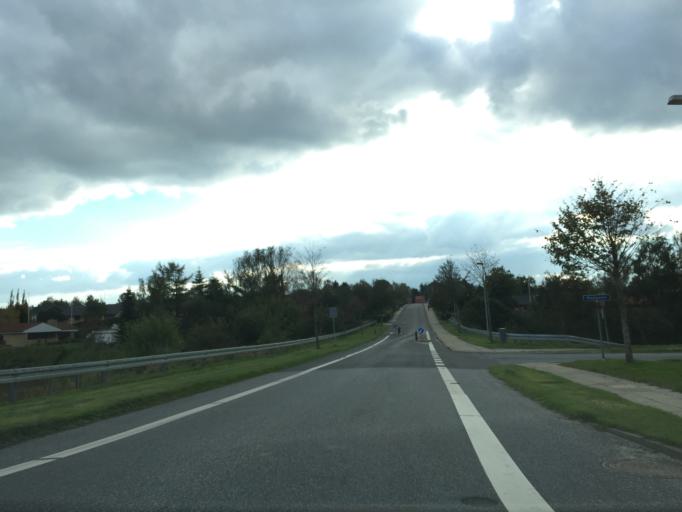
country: DK
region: Central Jutland
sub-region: Favrskov Kommune
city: Ulstrup
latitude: 56.3027
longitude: 9.7873
